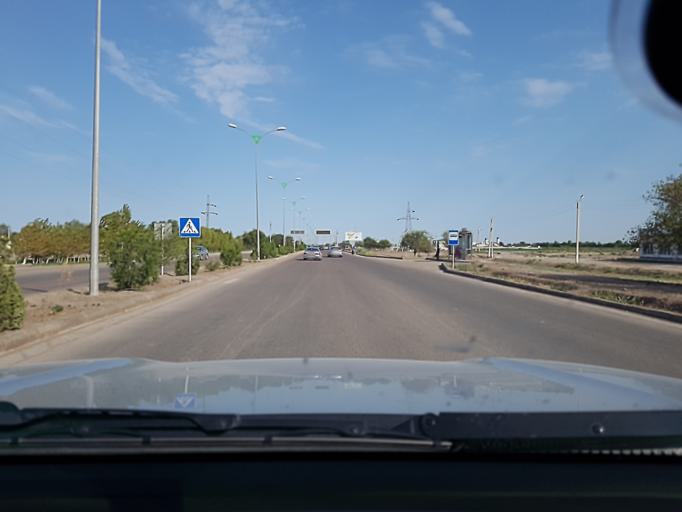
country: TM
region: Dasoguz
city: Koeneuergench
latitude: 42.3157
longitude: 59.1696
